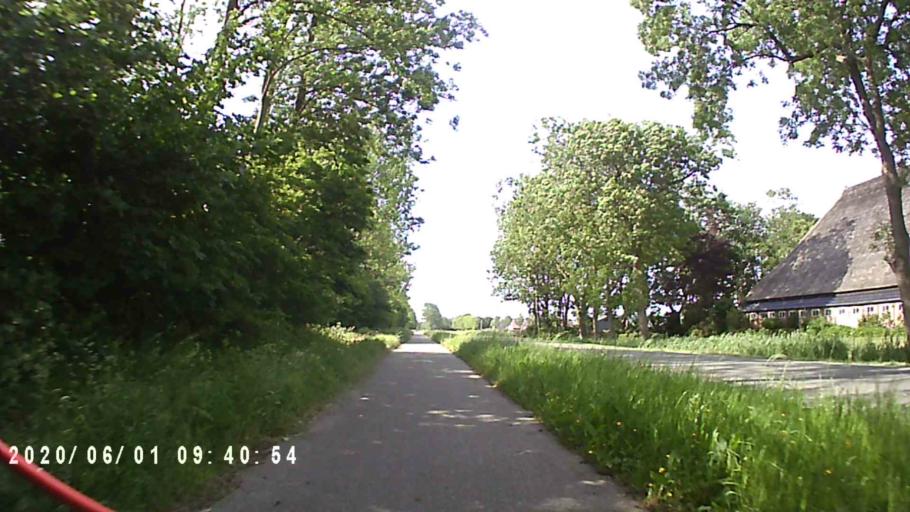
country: NL
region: Friesland
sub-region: Menameradiel
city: Berltsum
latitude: 53.2503
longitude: 5.6817
